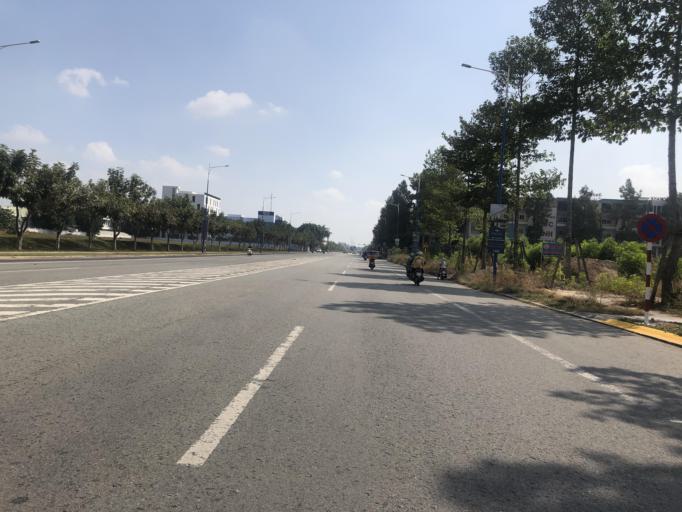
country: VN
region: Binh Duong
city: Thu Dau Mot
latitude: 11.0727
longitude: 106.6816
